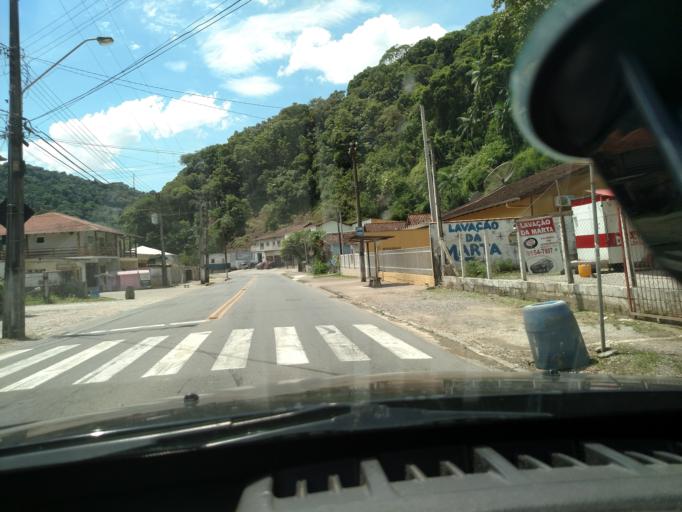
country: BR
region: Santa Catarina
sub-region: Blumenau
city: Blumenau
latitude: -26.9777
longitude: -49.0758
